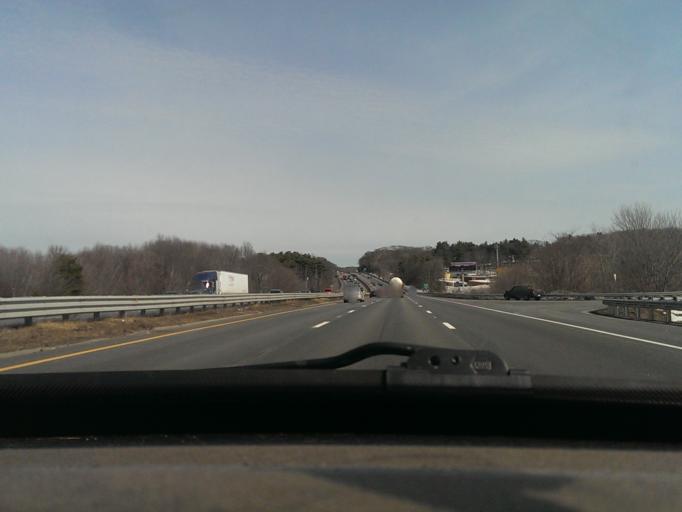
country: US
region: Massachusetts
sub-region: Worcester County
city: Auburn
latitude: 42.2026
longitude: -71.8227
